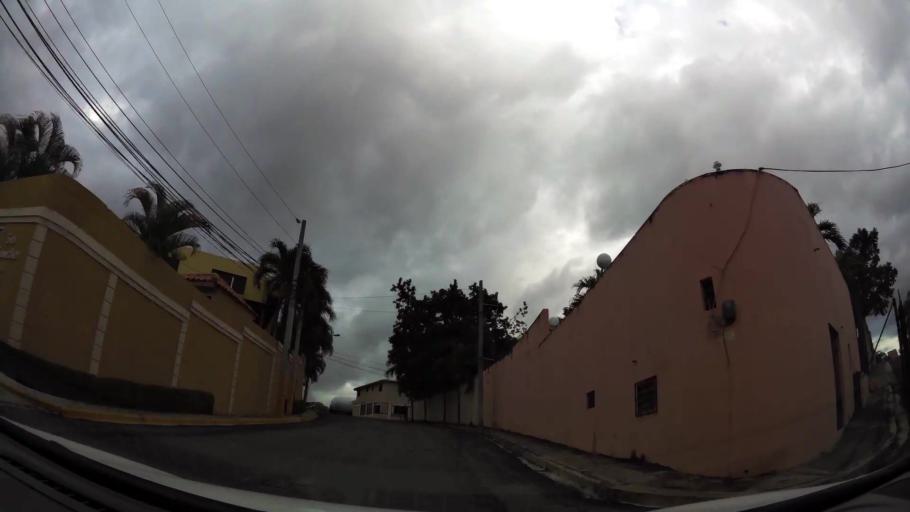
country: DO
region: Nacional
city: Santo Domingo
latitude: 18.5062
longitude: -69.9711
